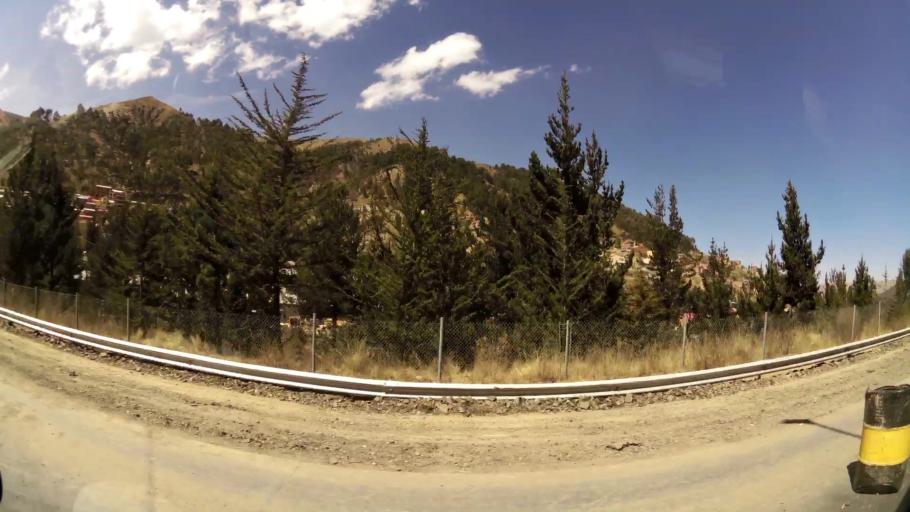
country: BO
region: La Paz
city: La Paz
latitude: -16.4603
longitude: -68.1492
